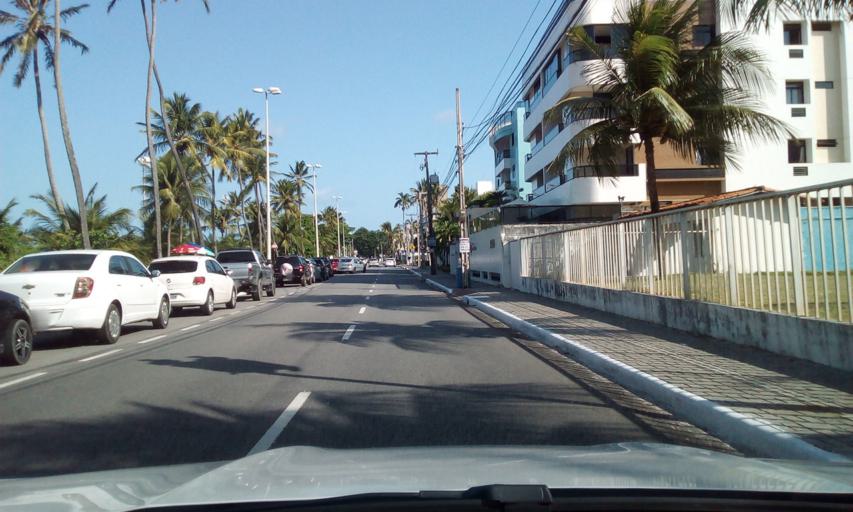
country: BR
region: Paraiba
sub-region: Joao Pessoa
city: Joao Pessoa
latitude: -7.1354
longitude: -34.8200
